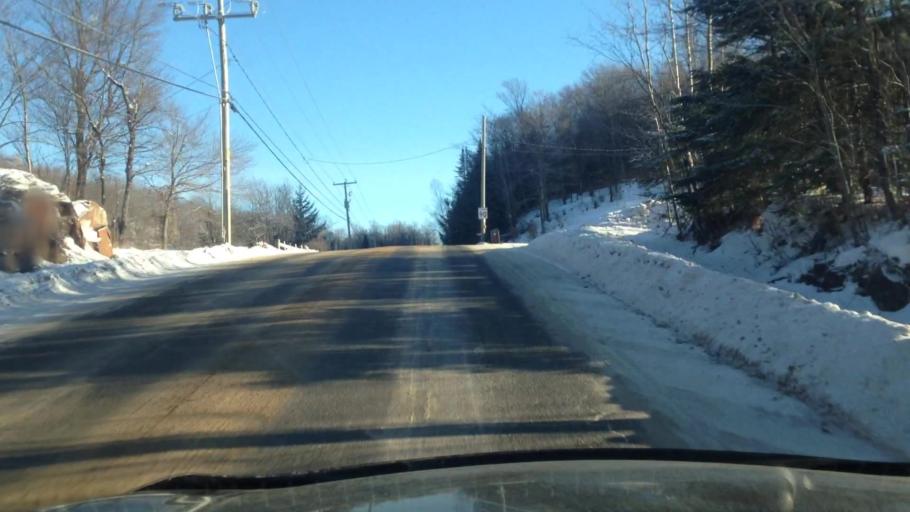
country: CA
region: Quebec
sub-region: Laurentides
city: Sainte-Agathe-des-Monts
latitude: 45.9342
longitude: -74.4497
